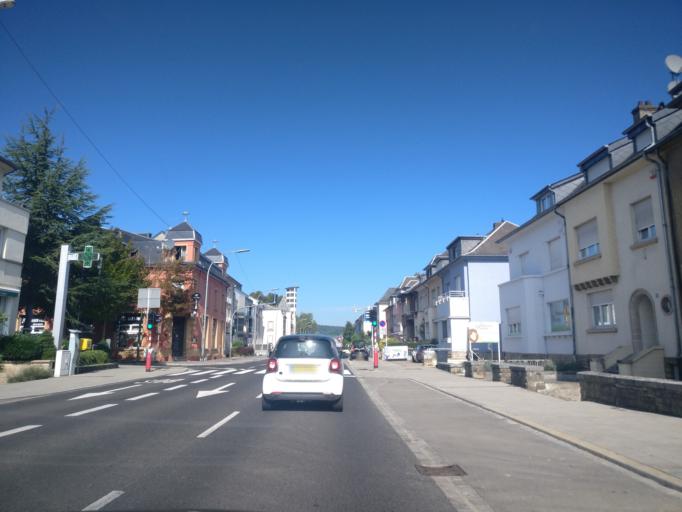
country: LU
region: Luxembourg
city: Helmsange
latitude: 49.6415
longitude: 6.1305
